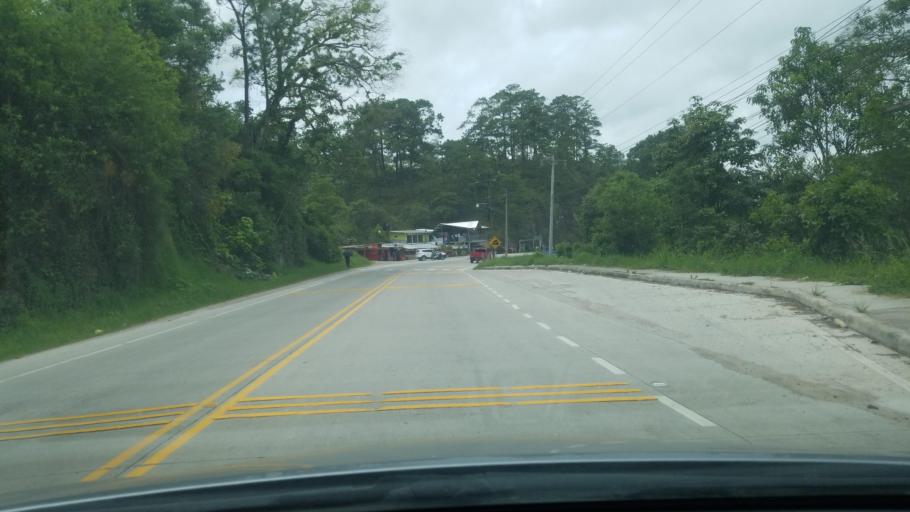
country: HN
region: Copan
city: Santa Rosa de Copan
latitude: 14.8057
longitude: -88.7746
